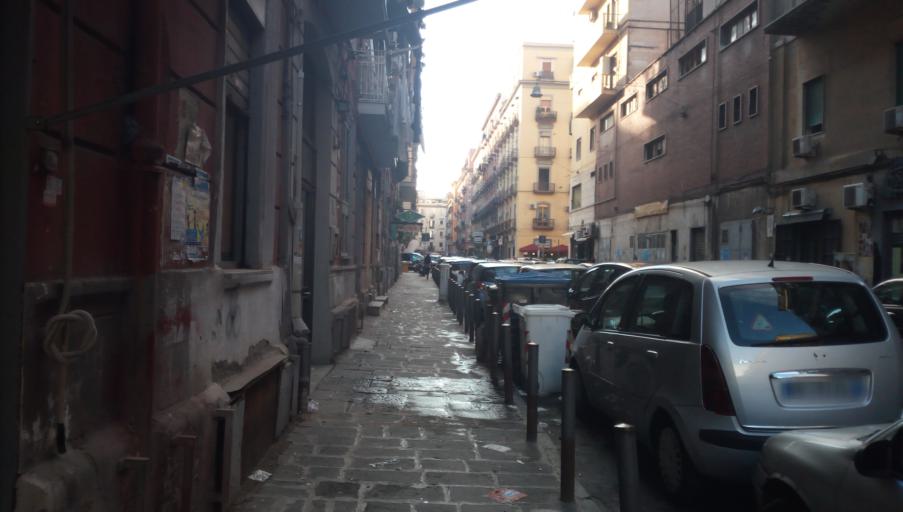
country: IT
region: Campania
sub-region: Provincia di Napoli
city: Napoli
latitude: 40.8550
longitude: 14.2722
